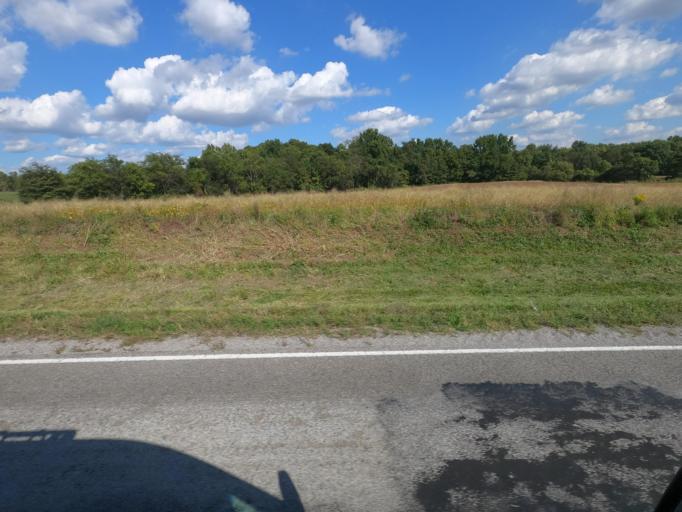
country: US
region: Illinois
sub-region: Massac County
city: Metropolis
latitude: 37.2564
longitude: -88.7495
